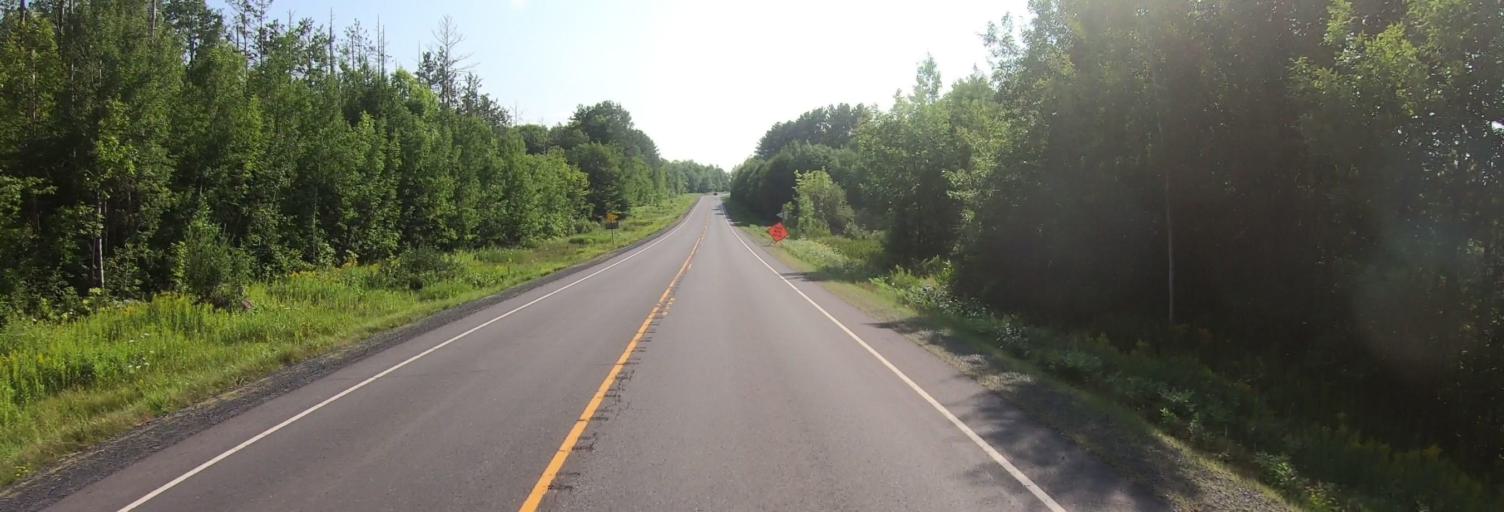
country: US
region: Wisconsin
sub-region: Iron County
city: Hurley
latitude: 46.4209
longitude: -90.2630
